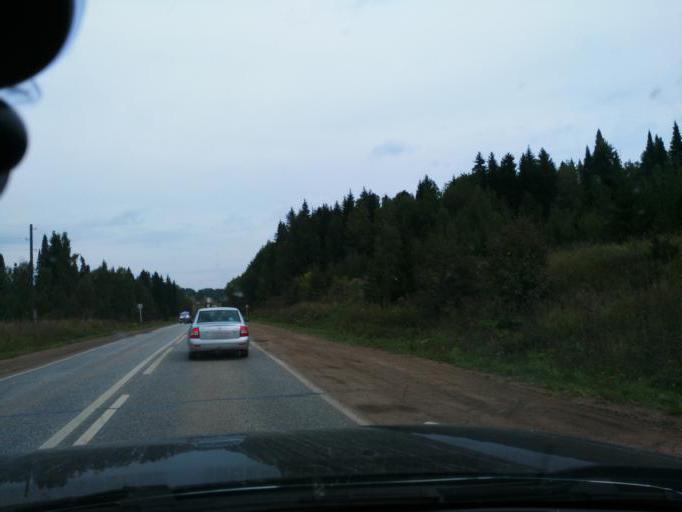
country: RU
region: Perm
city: Chernushka
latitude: 56.5677
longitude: 56.1214
